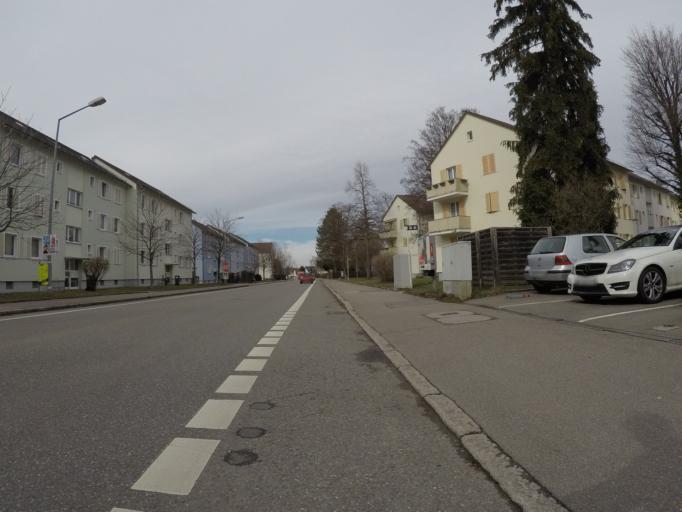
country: DE
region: Baden-Wuerttemberg
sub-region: Tuebingen Region
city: Reutlingen
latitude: 48.4993
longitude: 9.1909
